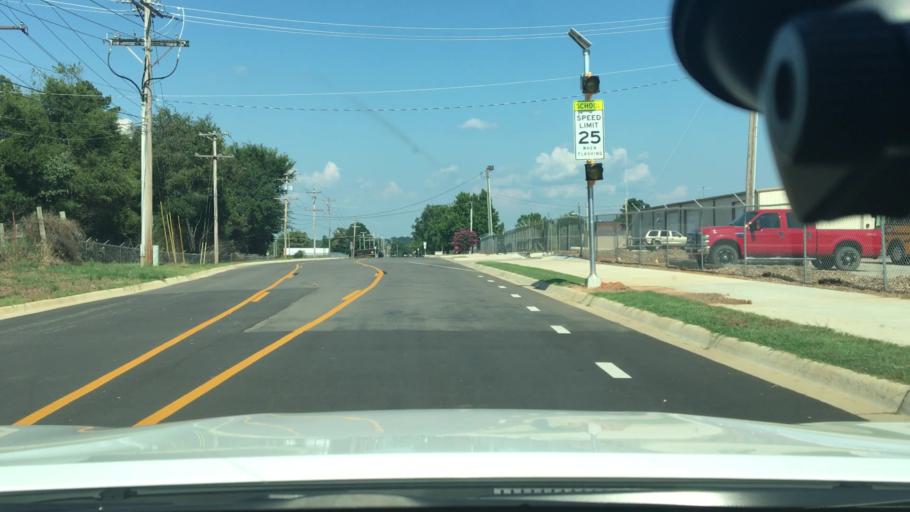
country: US
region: Arkansas
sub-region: Johnson County
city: Clarksville
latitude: 35.4619
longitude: -93.4931
